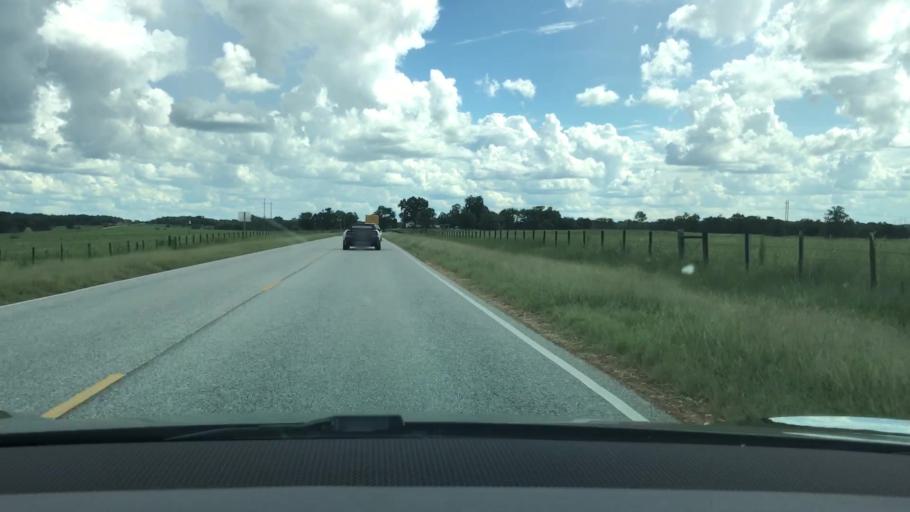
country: US
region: Alabama
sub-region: Montgomery County
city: Pike Road
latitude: 32.2658
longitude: -86.0992
